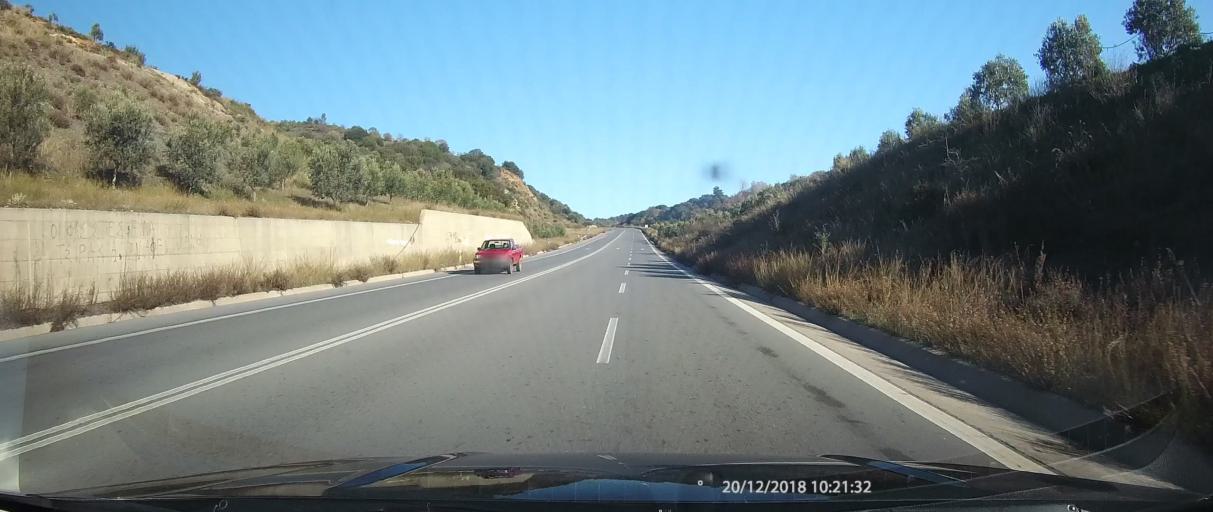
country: GR
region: Peloponnese
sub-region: Nomos Lakonias
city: Magoula
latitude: 37.1611
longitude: 22.4258
